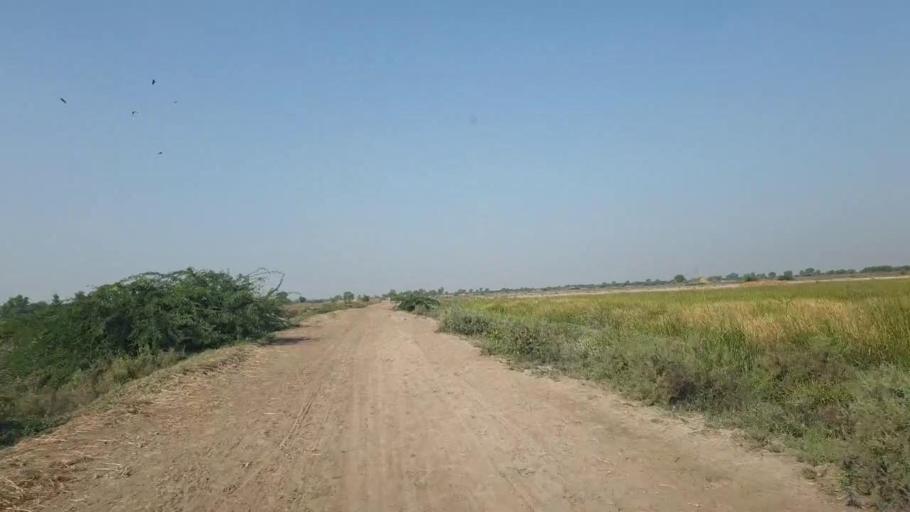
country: PK
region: Sindh
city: Badin
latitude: 24.5232
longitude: 68.7567
